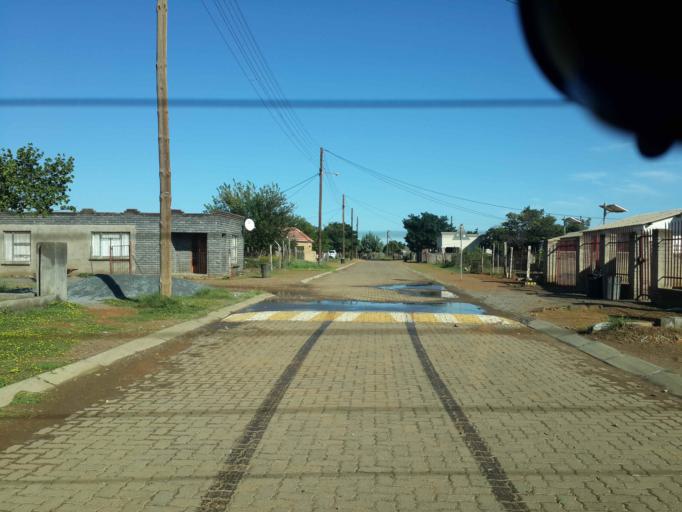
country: ZA
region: Northern Cape
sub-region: Siyanda District Municipality
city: Danielskuil
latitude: -28.1968
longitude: 23.5313
